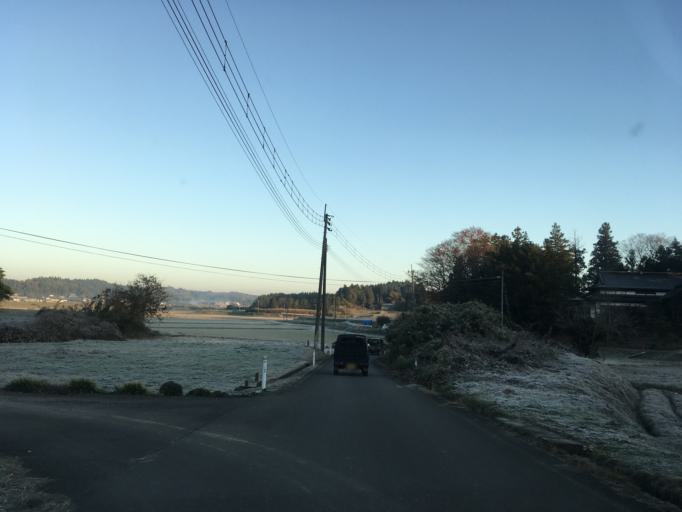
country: JP
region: Iwate
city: Ichinoseki
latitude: 38.7925
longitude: 141.1853
